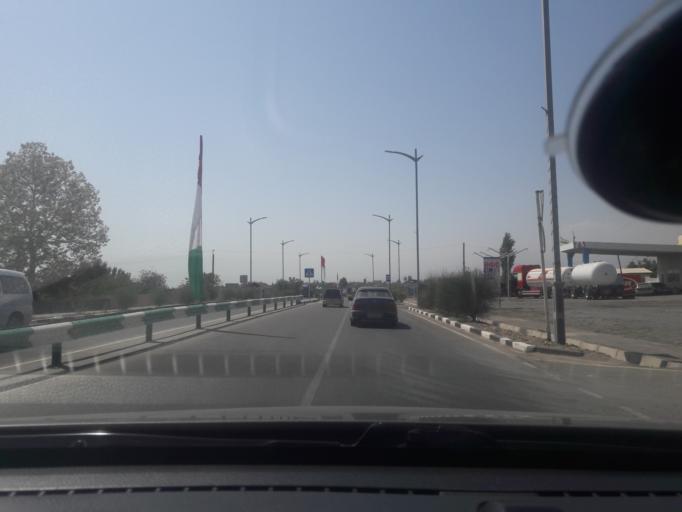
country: TJ
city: Shahrinav
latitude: 38.5613
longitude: 68.4378
